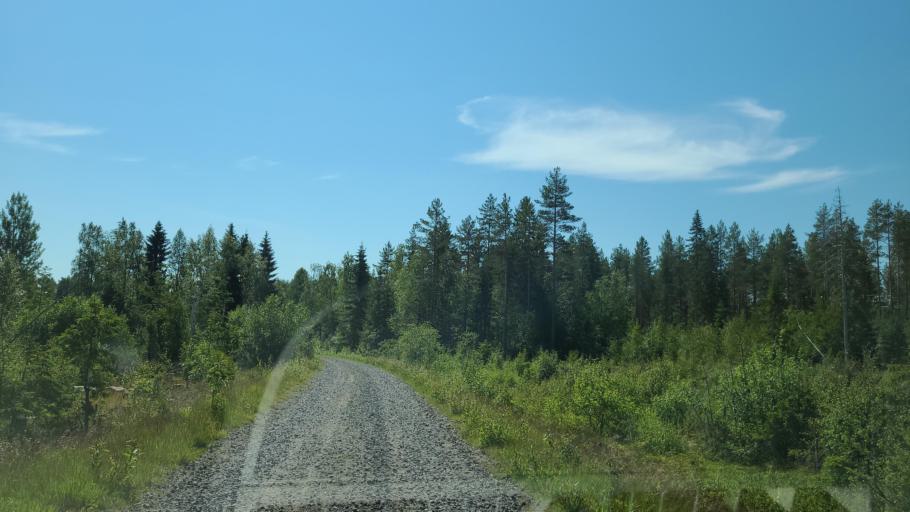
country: SE
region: Vaesterbotten
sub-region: Robertsfors Kommun
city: Robertsfors
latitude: 64.0921
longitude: 20.8356
